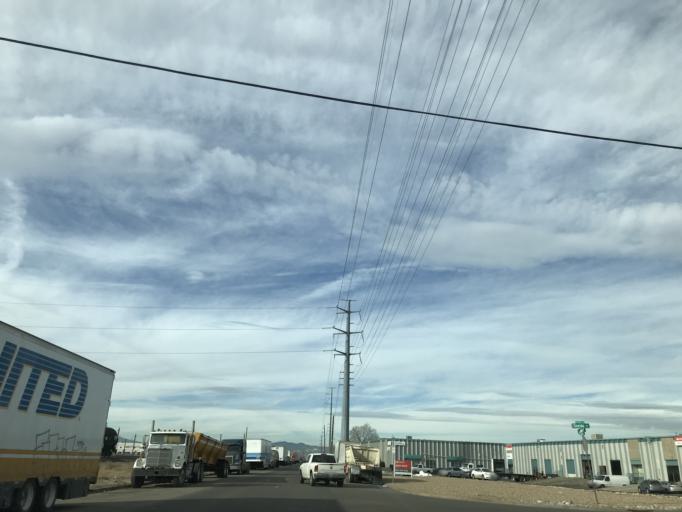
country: US
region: Colorado
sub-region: Adams County
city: Commerce City
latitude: 39.7734
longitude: -104.9080
